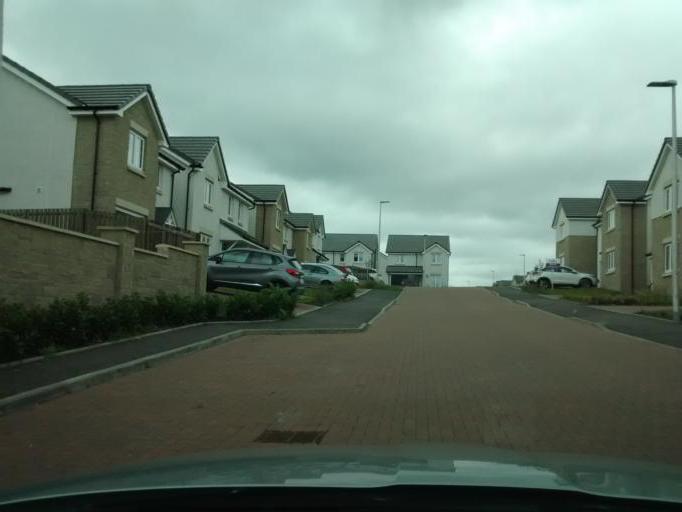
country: GB
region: Scotland
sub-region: West Lothian
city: Armadale
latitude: 55.8882
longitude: -3.6993
